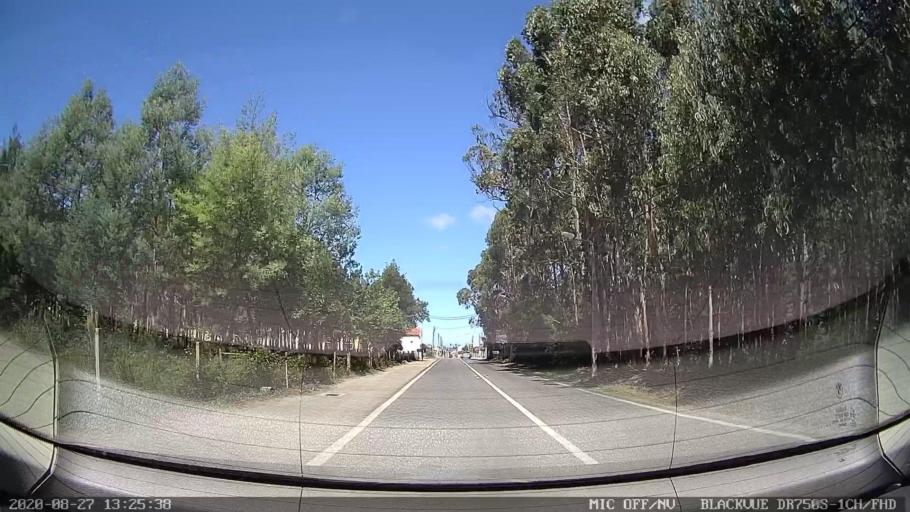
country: PT
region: Aveiro
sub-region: Vagos
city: Vagos
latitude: 40.5448
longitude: -8.6785
